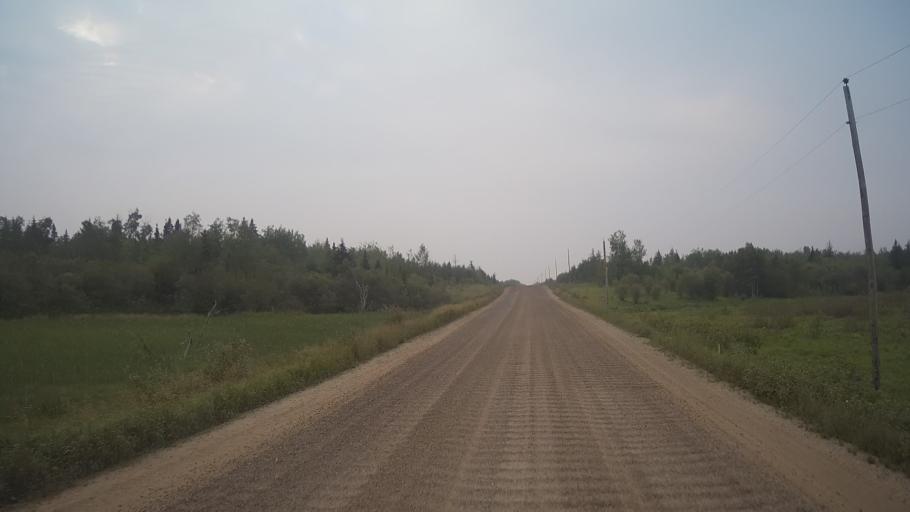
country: CA
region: Ontario
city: Hearst
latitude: 49.6328
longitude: -83.2783
